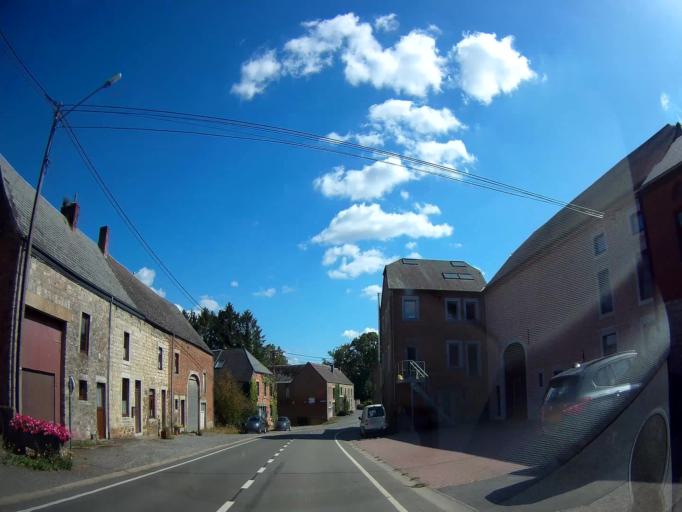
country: FR
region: Champagne-Ardenne
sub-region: Departement des Ardennes
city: Fromelennes
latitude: 50.1691
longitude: 4.8832
